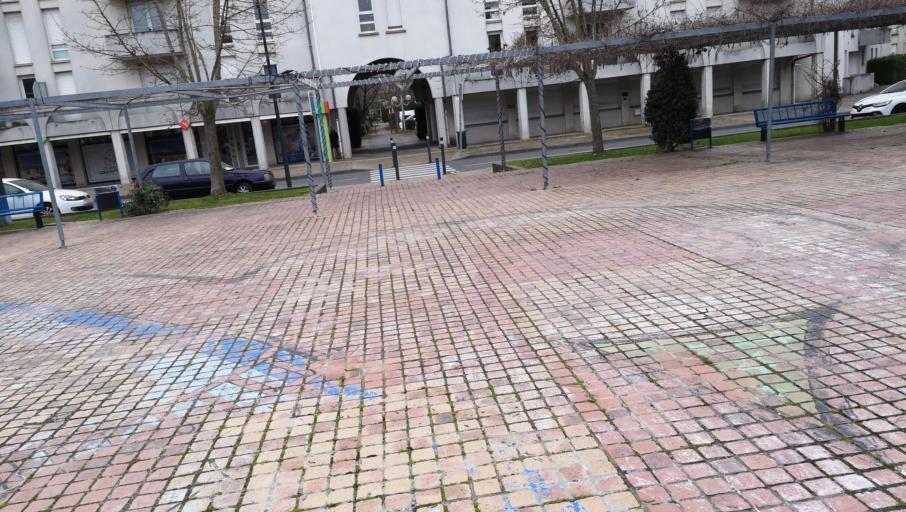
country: FR
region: Midi-Pyrenees
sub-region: Departement de la Haute-Garonne
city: Blagnac
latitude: 43.6414
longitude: 1.3799
